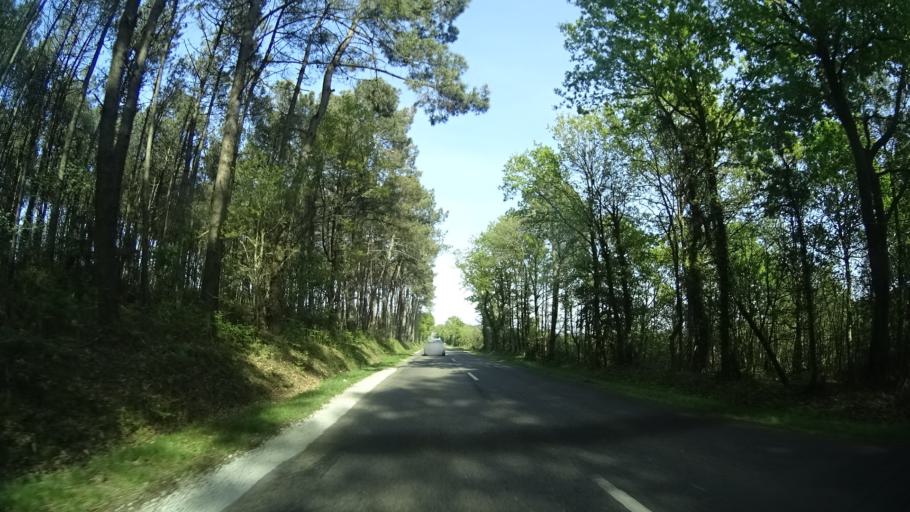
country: FR
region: Brittany
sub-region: Departement du Morbihan
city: Allaire
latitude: 47.6121
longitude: -2.1617
